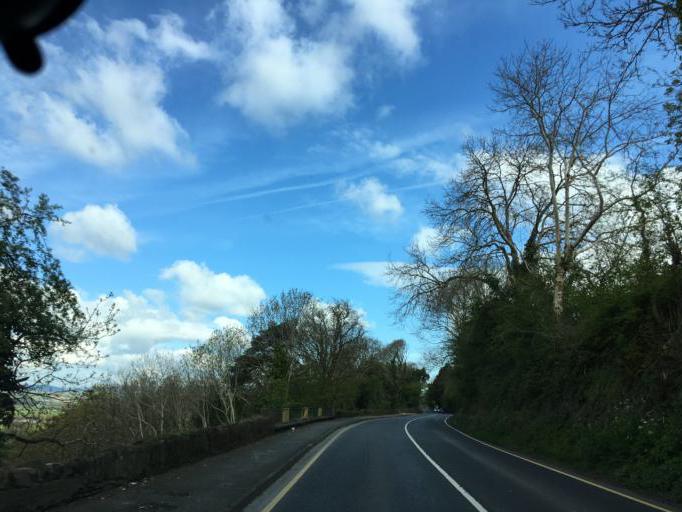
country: IE
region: Leinster
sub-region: Loch Garman
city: New Ross
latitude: 52.4054
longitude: -6.9385
